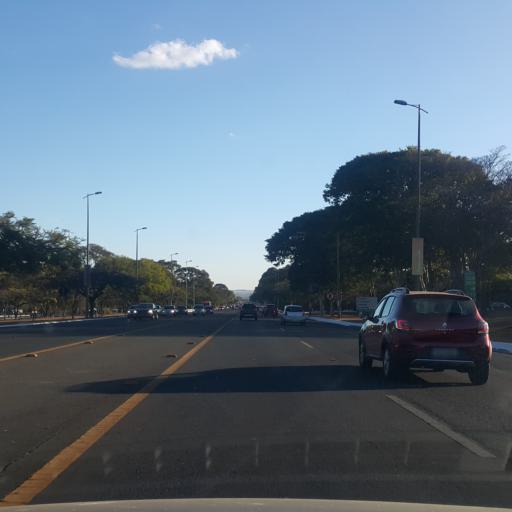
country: BR
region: Federal District
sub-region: Brasilia
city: Brasilia
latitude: -15.8230
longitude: -47.9091
